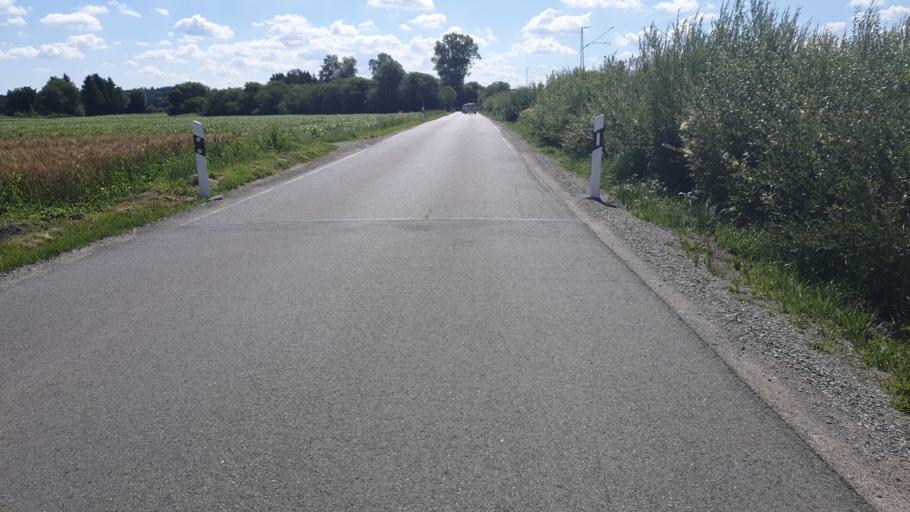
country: DE
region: Bavaria
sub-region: Upper Bavaria
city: Puchheim
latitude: 48.1672
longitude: 11.3710
